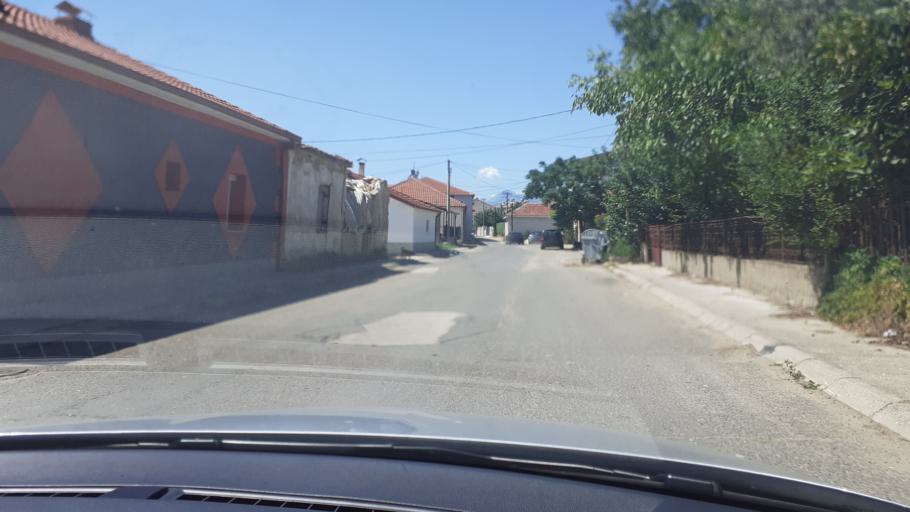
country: MK
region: Bogdanci
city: Bogdanci
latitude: 41.2002
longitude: 22.5764
